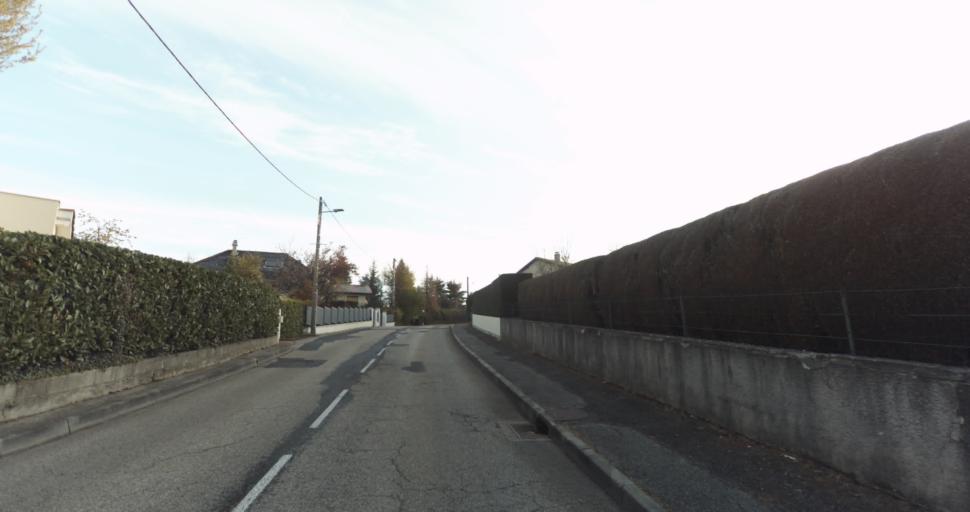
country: FR
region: Rhone-Alpes
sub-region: Departement de la Loire
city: Saint-Jean-Bonnefonds
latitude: 45.4502
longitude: 4.4326
